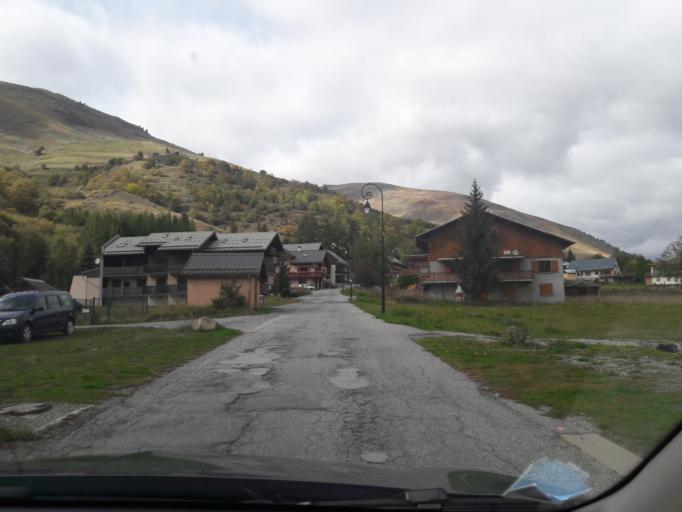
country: FR
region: Rhone-Alpes
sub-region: Departement de la Savoie
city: Valloire
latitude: 45.1463
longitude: 6.4182
